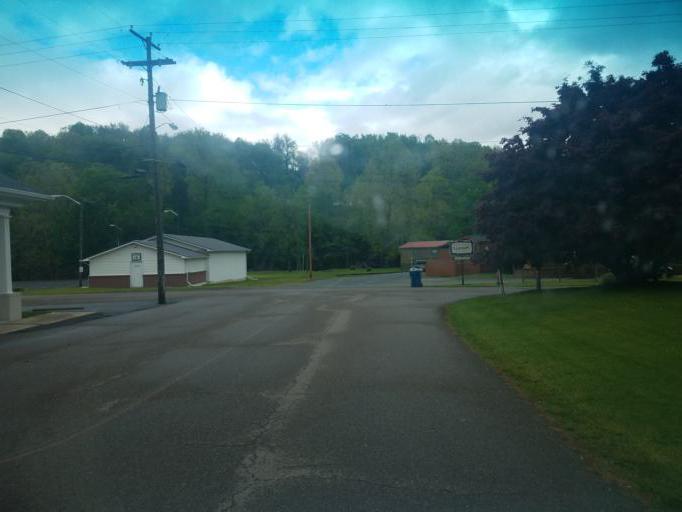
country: US
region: Virginia
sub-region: Washington County
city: Emory
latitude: 36.6356
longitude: -81.7883
